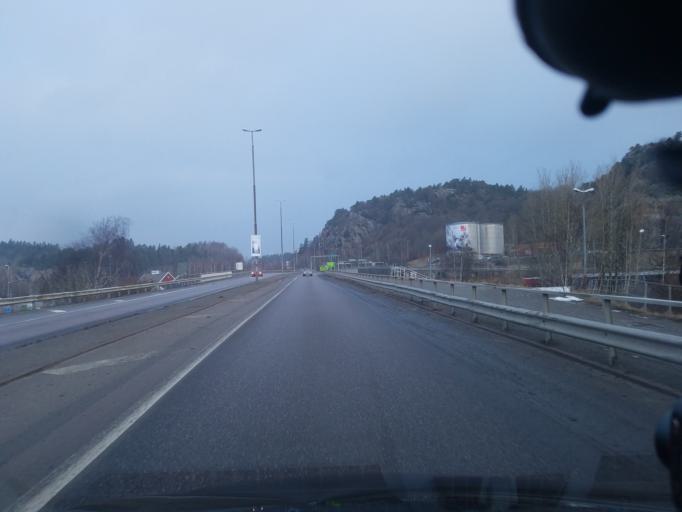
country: SE
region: Vaestra Goetaland
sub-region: Uddevalla Kommun
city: Uddevalla
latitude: 58.3540
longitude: 11.9138
